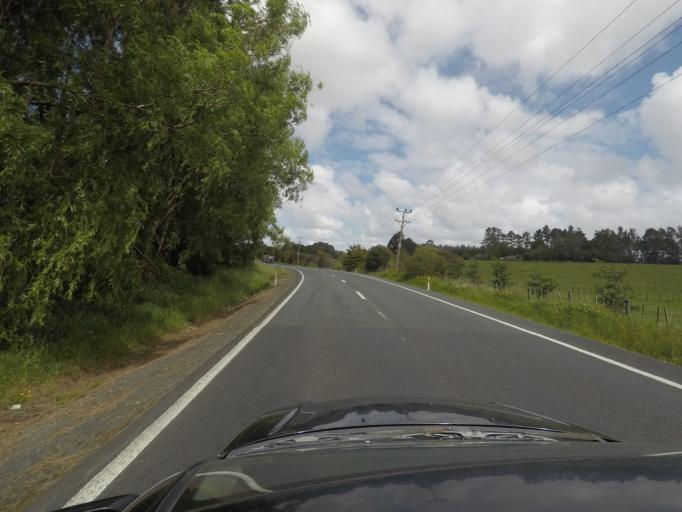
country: NZ
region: Auckland
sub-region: Auckland
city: Parakai
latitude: -36.6300
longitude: 174.5162
